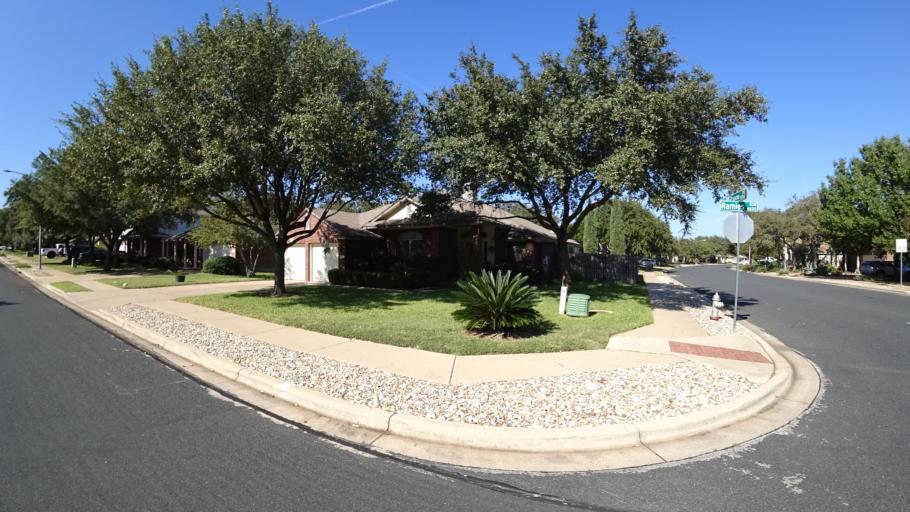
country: US
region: Texas
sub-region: Travis County
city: Shady Hollow
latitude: 30.2001
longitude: -97.8590
